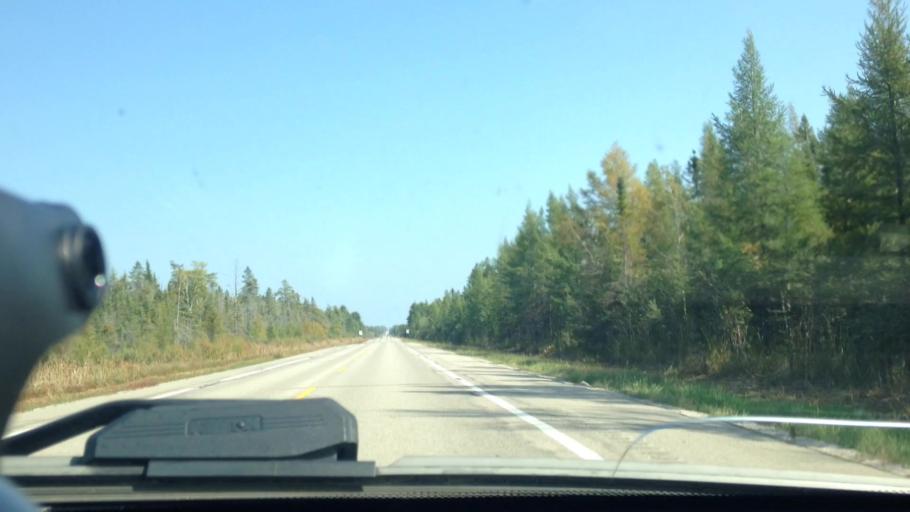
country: US
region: Michigan
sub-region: Luce County
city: Newberry
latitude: 46.3035
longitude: -85.3422
